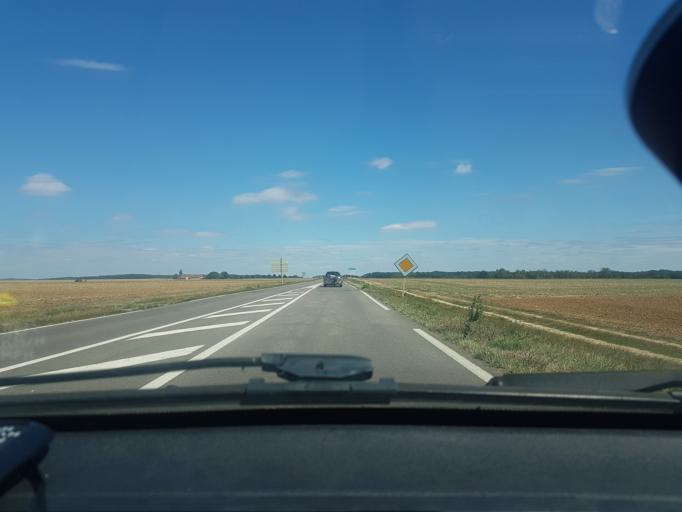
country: FR
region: Bourgogne
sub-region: Departement de la Cote-d'Or
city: Arc-sur-Tille
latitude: 47.3482
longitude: 5.2001
